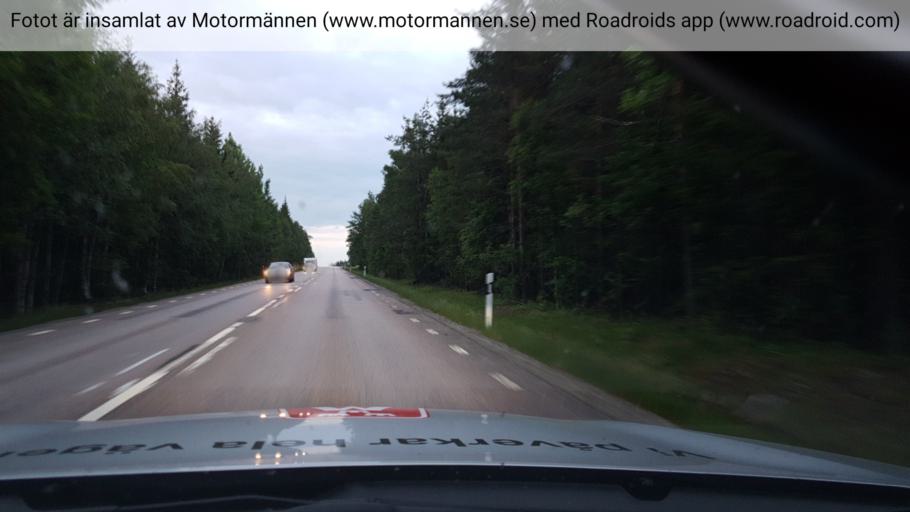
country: SE
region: Vaestmanland
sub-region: Fagersta Kommun
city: Fagersta
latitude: 59.9418
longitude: 15.7372
